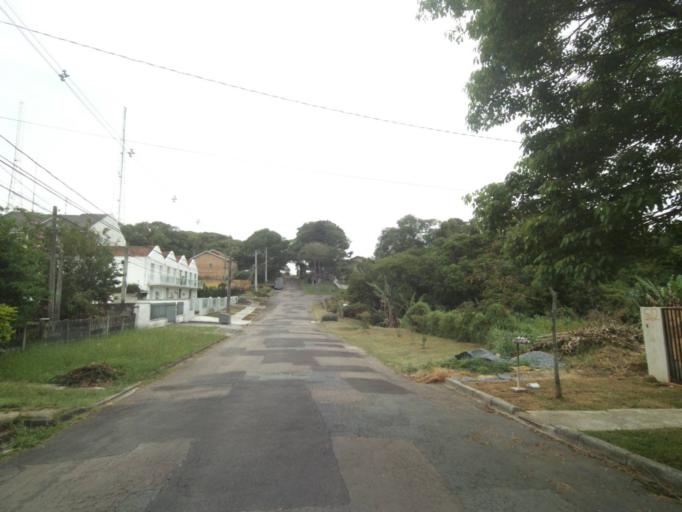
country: BR
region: Parana
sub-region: Curitiba
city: Curitiba
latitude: -25.3959
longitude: -49.2809
